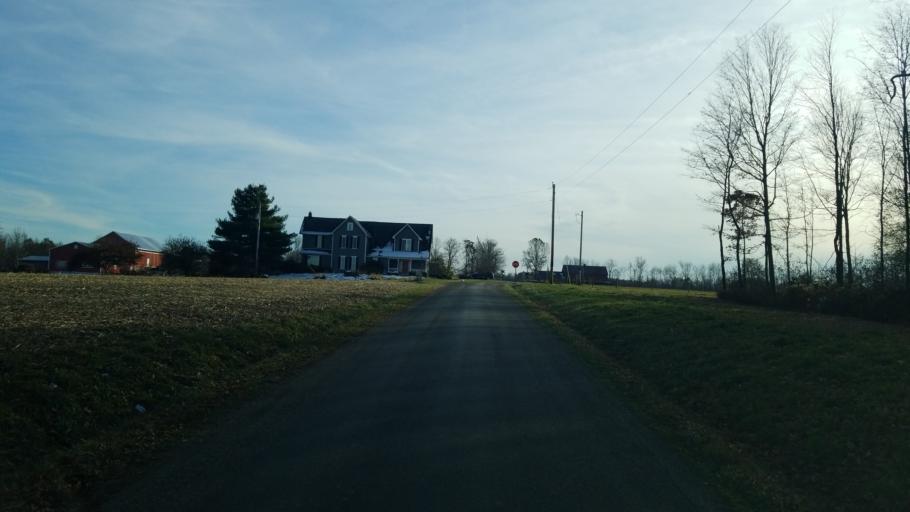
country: US
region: Ohio
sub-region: Ashland County
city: Ashland
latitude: 40.7559
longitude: -82.2884
